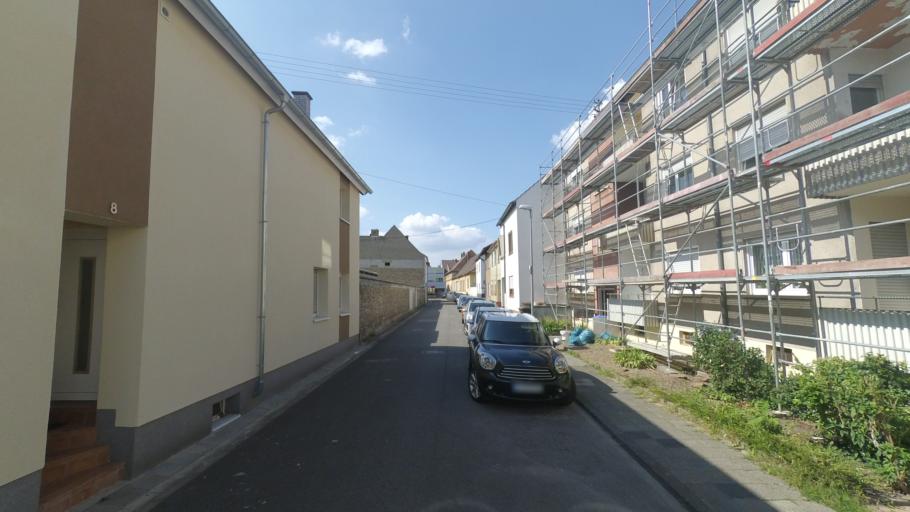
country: DE
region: Rheinland-Pfalz
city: Frankenthal
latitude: 49.5196
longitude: 8.4041
